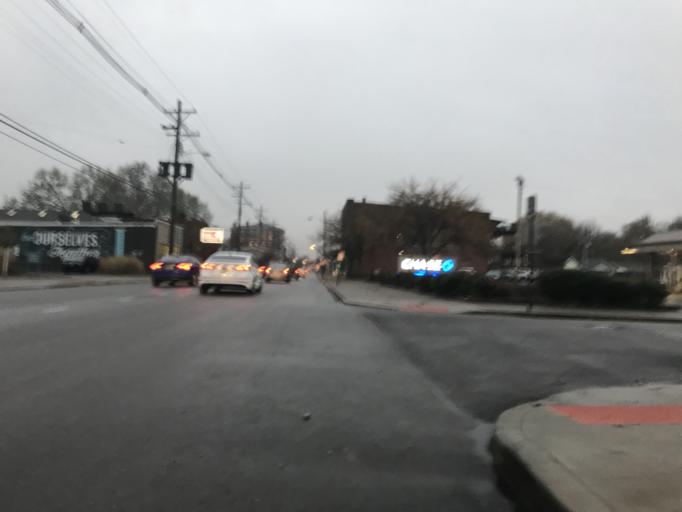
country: US
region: Kentucky
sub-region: Jefferson County
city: Louisville
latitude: 38.2328
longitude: -85.7416
